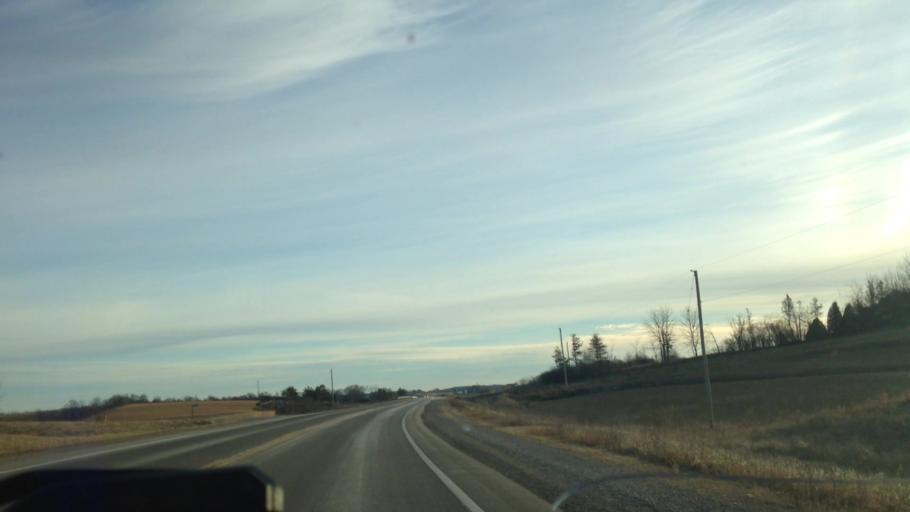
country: US
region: Wisconsin
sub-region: Dodge County
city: Theresa
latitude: 43.5364
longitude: -88.4388
